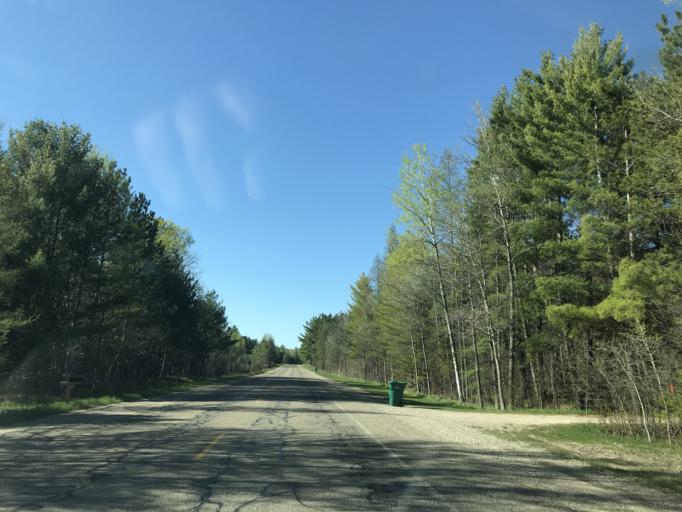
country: US
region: Michigan
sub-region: Crawford County
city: Grayling
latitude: 44.7587
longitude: -84.7535
